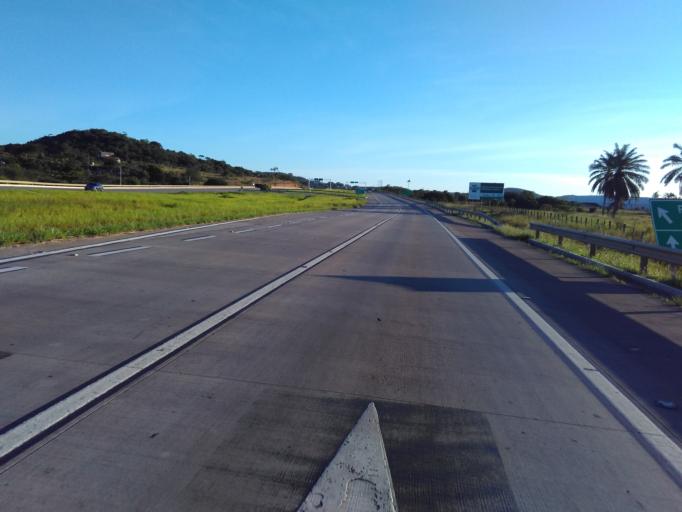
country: BR
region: Sergipe
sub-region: Nossa Senhora Do Socorro
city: Nossa Senhora do Socorro
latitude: -10.9173
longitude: -37.1669
